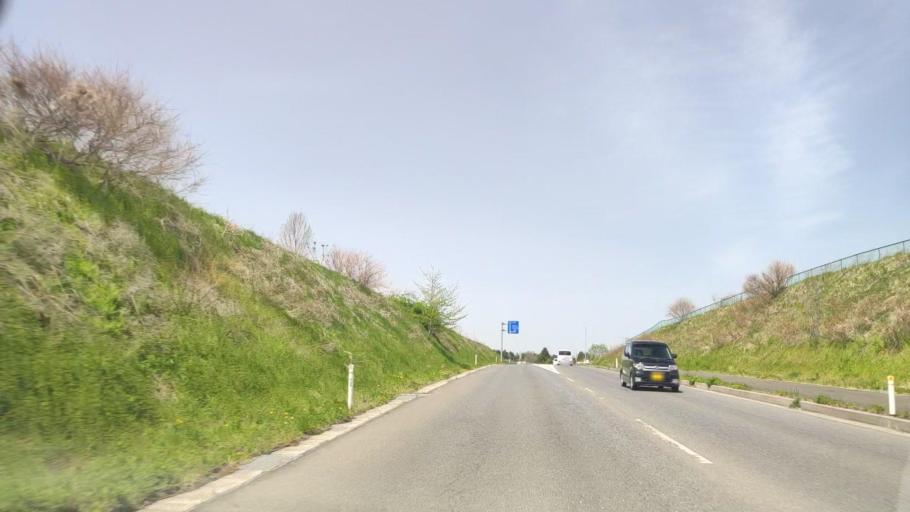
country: JP
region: Aomori
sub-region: Hachinohe Shi
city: Uchimaru
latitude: 40.5269
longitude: 141.4101
